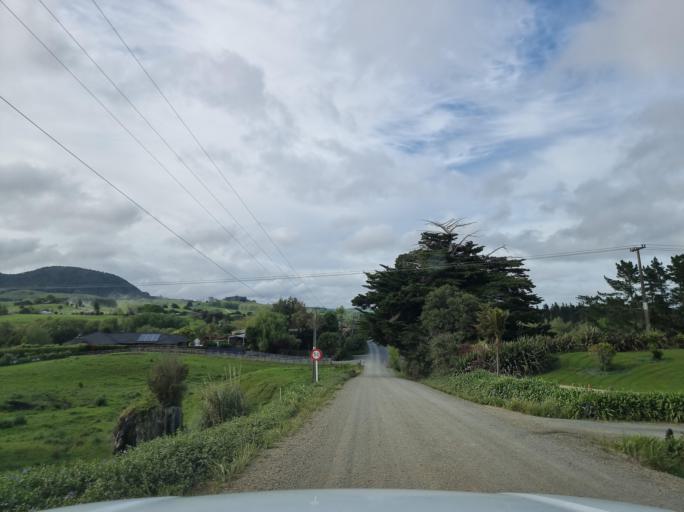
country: NZ
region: Northland
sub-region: Whangarei
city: Ruakaka
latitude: -36.1000
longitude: 174.3668
